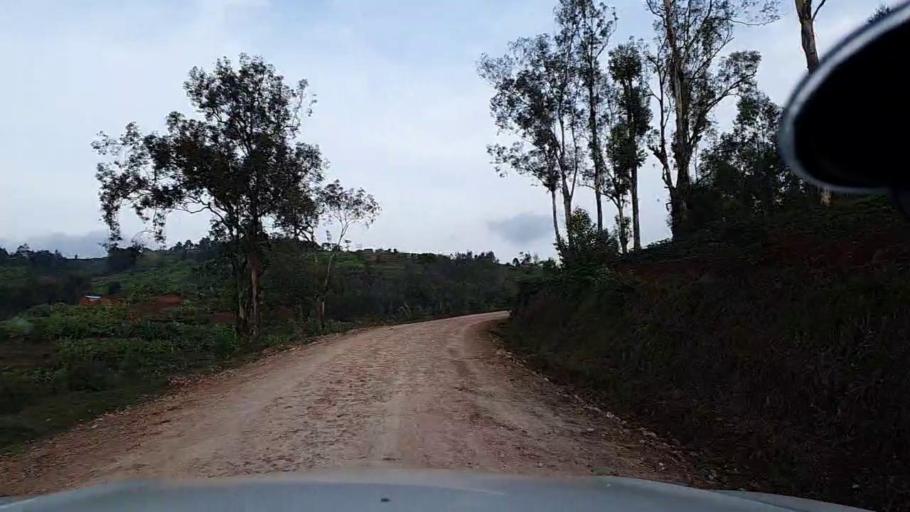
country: RW
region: Southern Province
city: Nyanza
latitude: -2.2110
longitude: 29.6276
